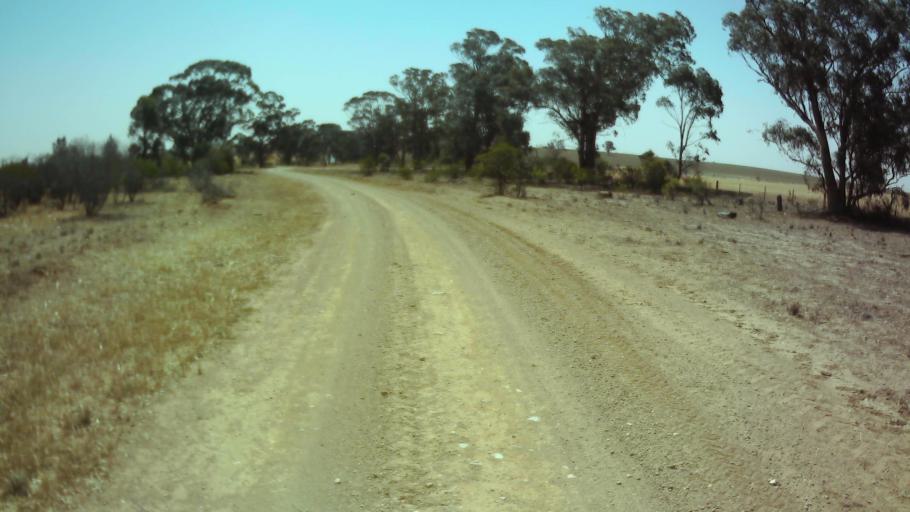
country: AU
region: New South Wales
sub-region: Weddin
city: Grenfell
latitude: -33.9113
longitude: 147.7682
